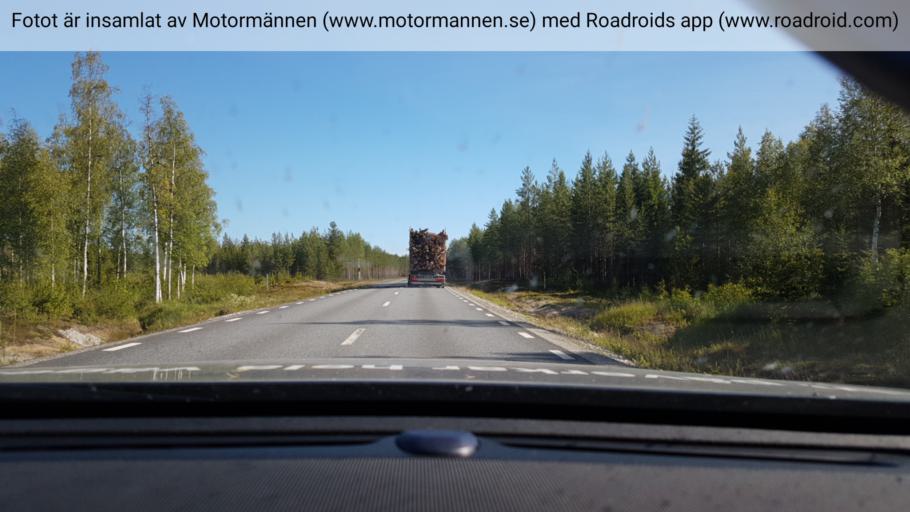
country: SE
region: Vaesterbotten
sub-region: Bjurholms Kommun
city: Bjurholm
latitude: 64.3150
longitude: 19.1607
